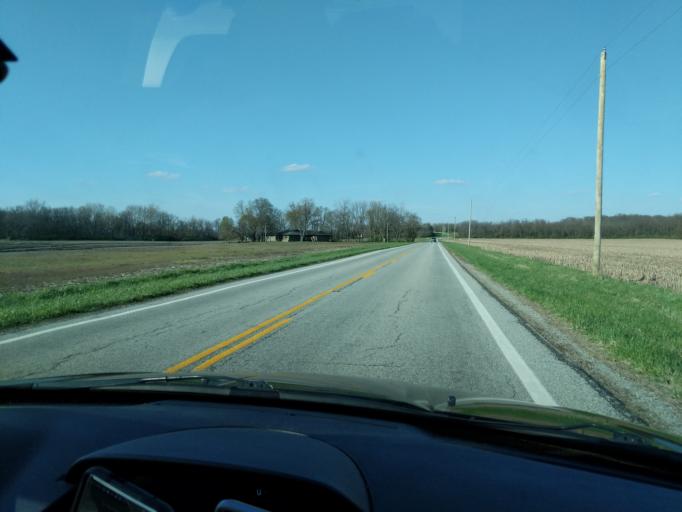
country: US
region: Ohio
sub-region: Champaign County
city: Urbana
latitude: 40.0800
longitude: -83.7991
